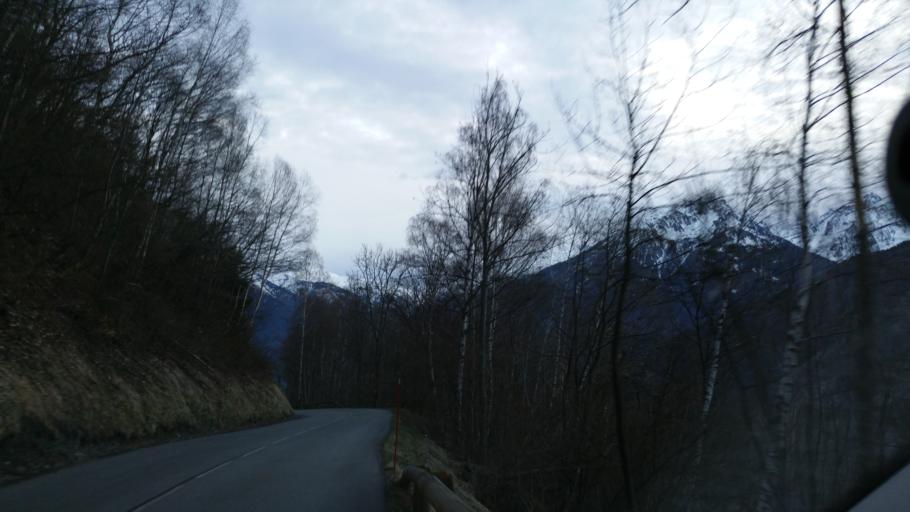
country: FR
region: Rhone-Alpes
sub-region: Departement de la Savoie
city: La Chambre
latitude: 45.3870
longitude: 6.3313
